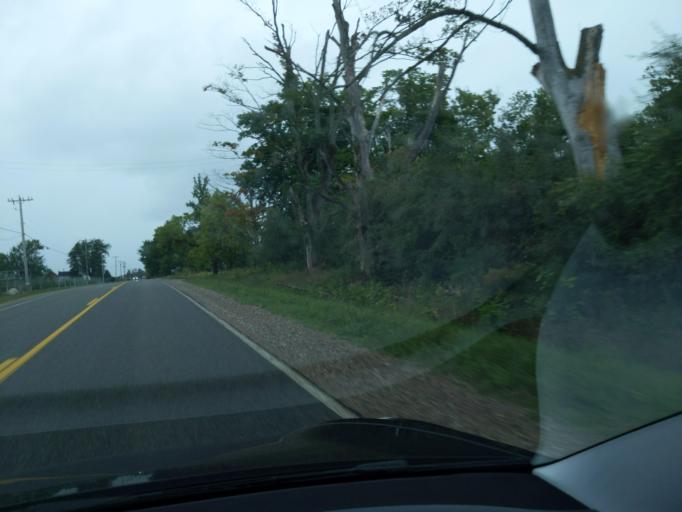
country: US
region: Michigan
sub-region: Antrim County
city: Elk Rapids
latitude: 44.8232
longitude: -85.4049
